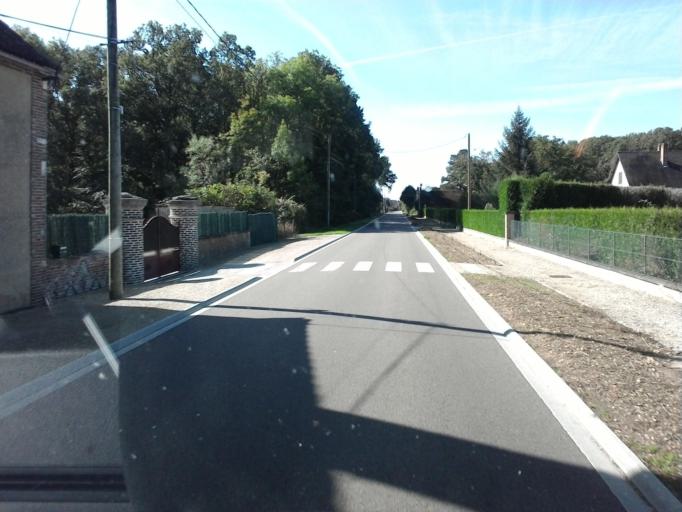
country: FR
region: Champagne-Ardenne
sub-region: Departement de l'Aube
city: Chaource
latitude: 47.9765
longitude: 4.0504
